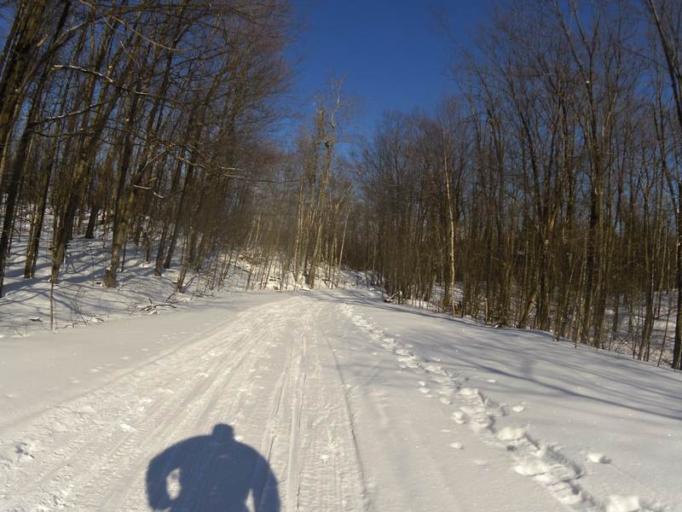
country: CA
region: Quebec
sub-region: Outaouais
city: Wakefield
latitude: 45.5293
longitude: -75.9304
